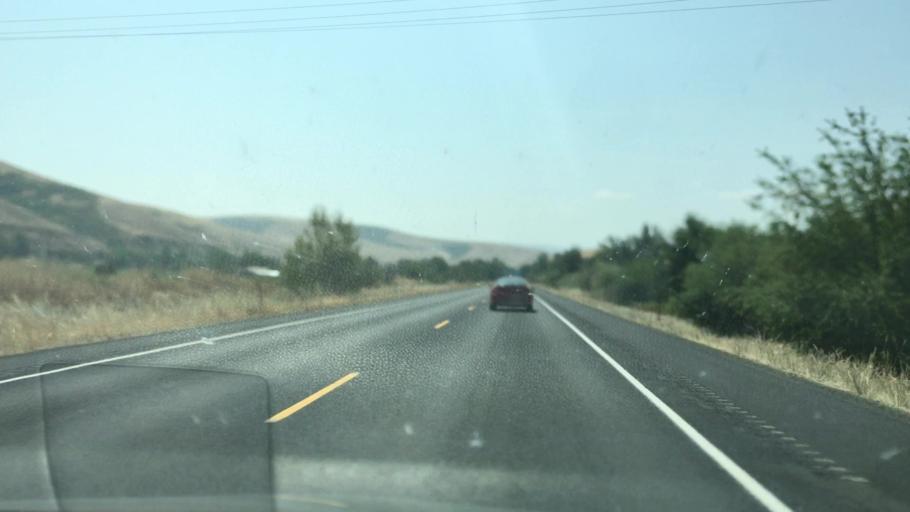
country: US
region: Idaho
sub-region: Nez Perce County
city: Lapwai
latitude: 46.4342
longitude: -116.8081
